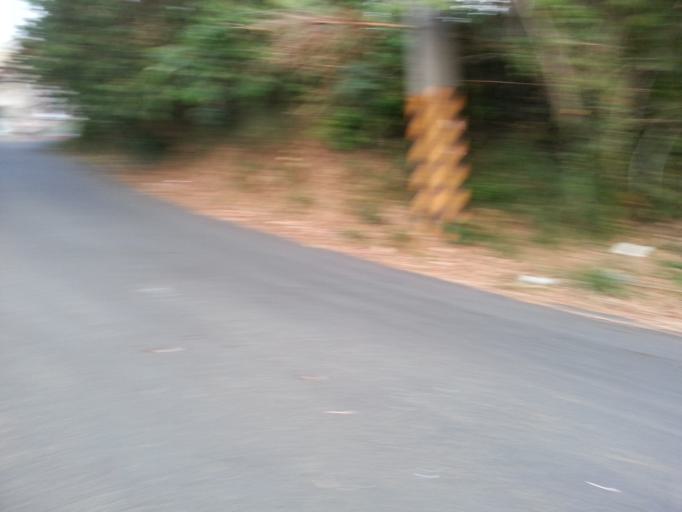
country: TW
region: Taiwan
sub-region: Hsinchu
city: Hsinchu
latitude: 24.7555
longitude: 120.9525
